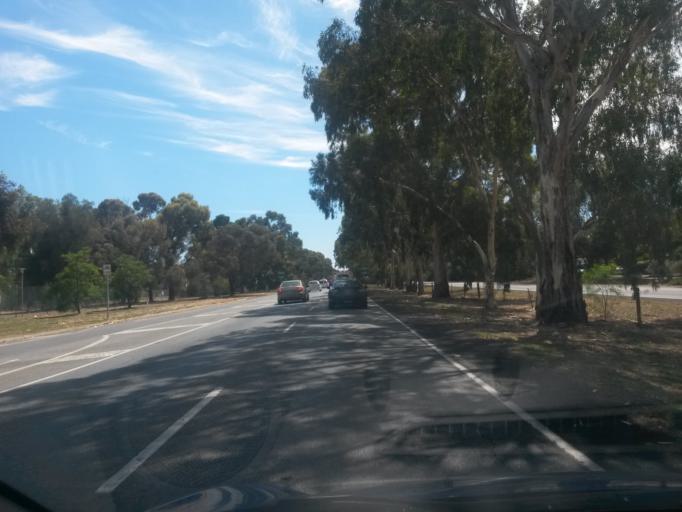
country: AU
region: South Australia
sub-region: Salisbury
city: Salisbury
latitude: -34.7857
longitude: 138.6520
